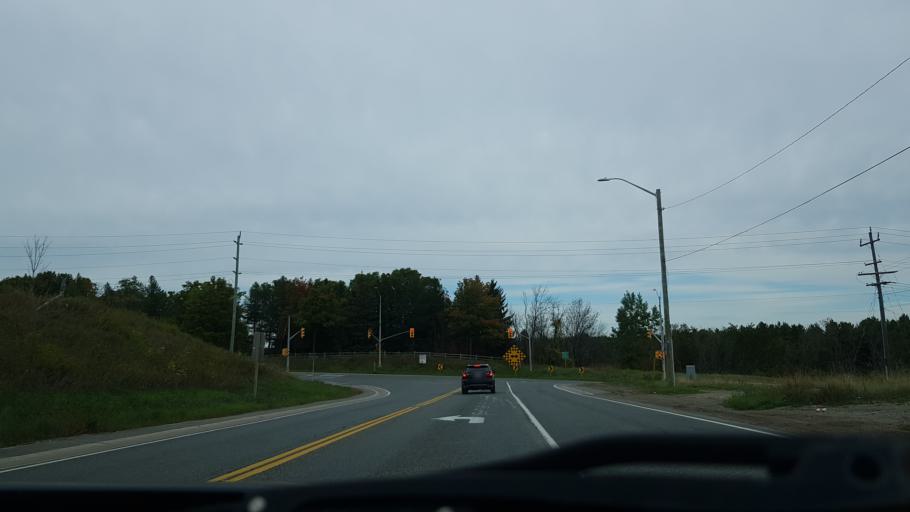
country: CA
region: Ontario
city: Orangeville
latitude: 43.9164
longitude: -79.9321
